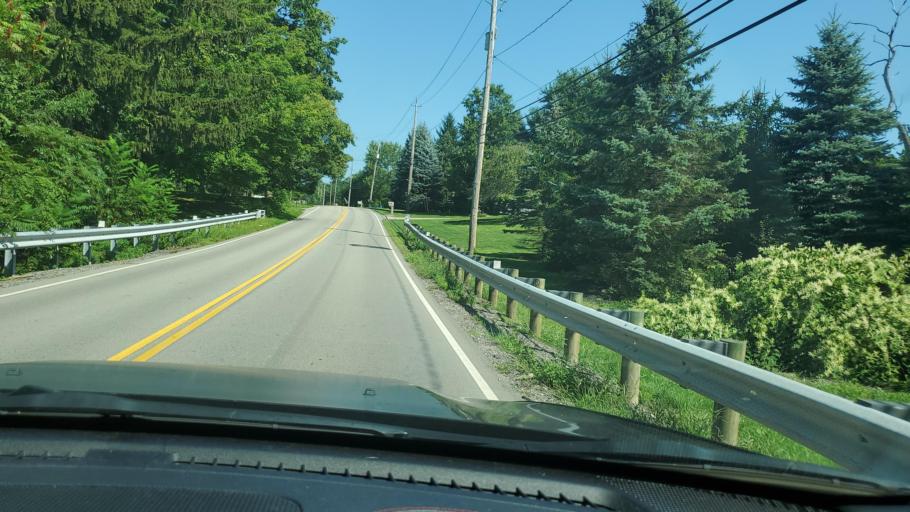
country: US
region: Ohio
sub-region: Trumbull County
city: Girard
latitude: 41.1739
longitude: -80.6911
